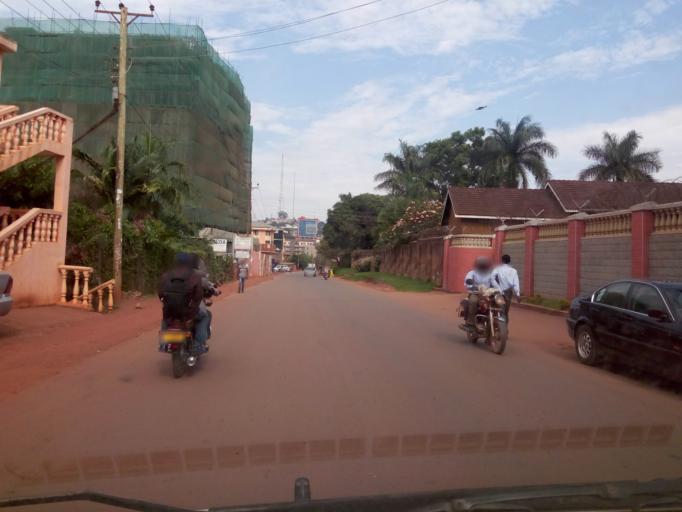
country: UG
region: Central Region
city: Kampala Central Division
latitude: 0.3430
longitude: 32.5826
